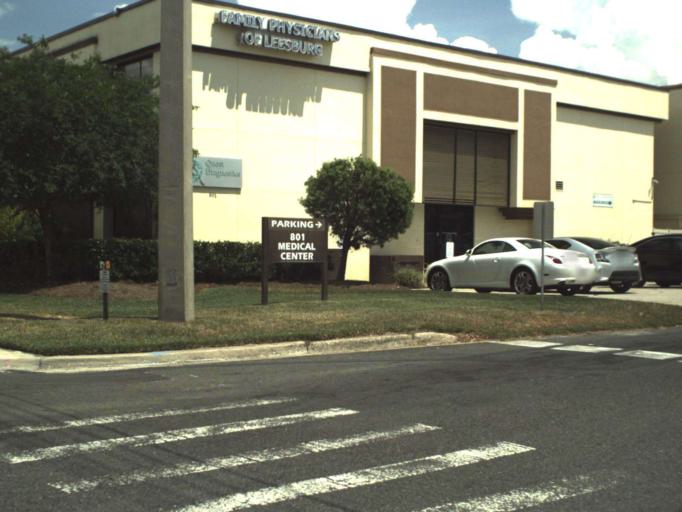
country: US
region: Florida
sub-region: Lake County
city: Leesburg
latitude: 28.8065
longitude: -81.8670
